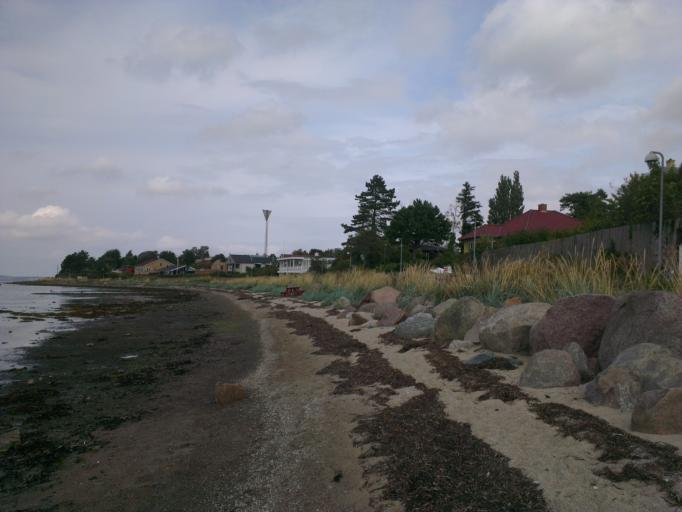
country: DK
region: Capital Region
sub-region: Frederikssund Kommune
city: Frederikssund
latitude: 55.8466
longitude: 12.0440
